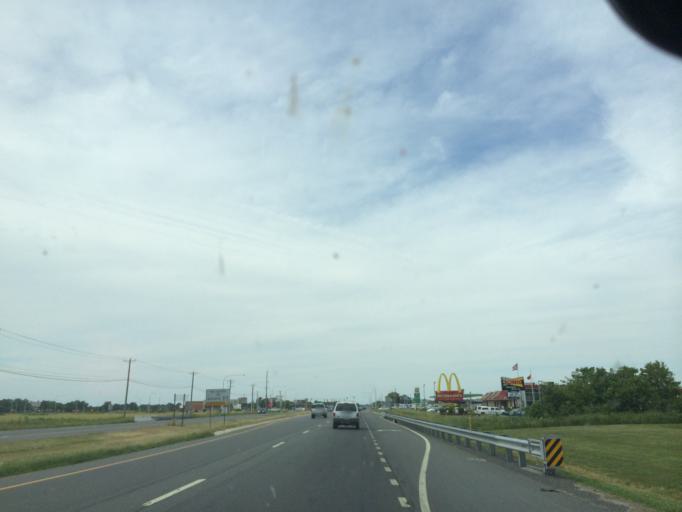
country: US
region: Delaware
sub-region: Sussex County
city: Bridgeville
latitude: 38.7203
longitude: -75.5898
